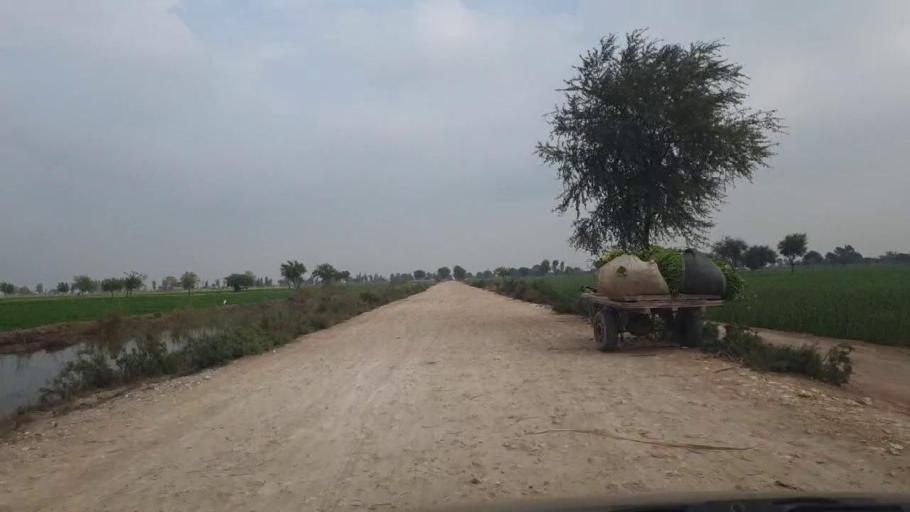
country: PK
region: Sindh
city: Shahdadpur
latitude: 25.8906
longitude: 68.6950
